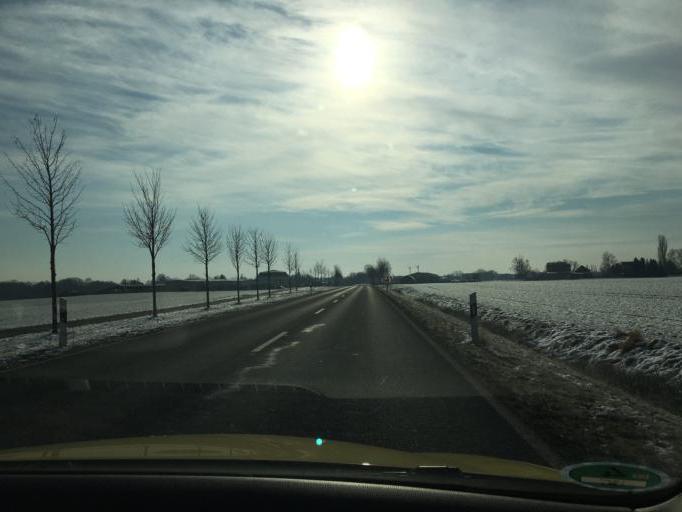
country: DE
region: Saxony
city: Bad Lausick
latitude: 51.1568
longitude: 12.6319
